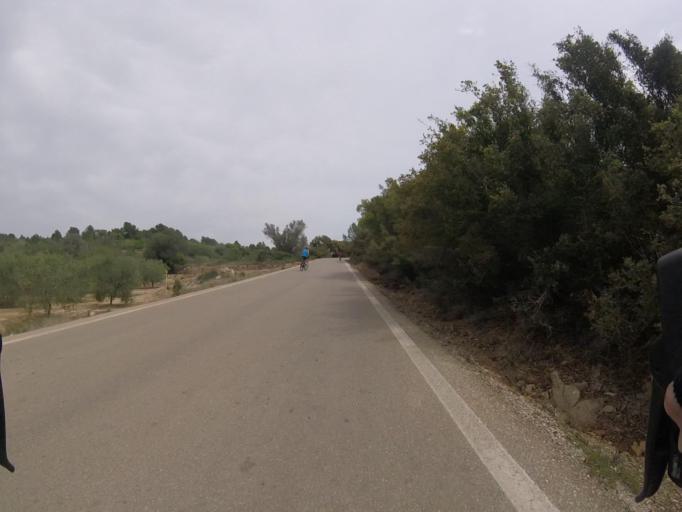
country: ES
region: Valencia
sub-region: Provincia de Castello
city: Cabanes
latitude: 40.1558
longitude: 0.0601
